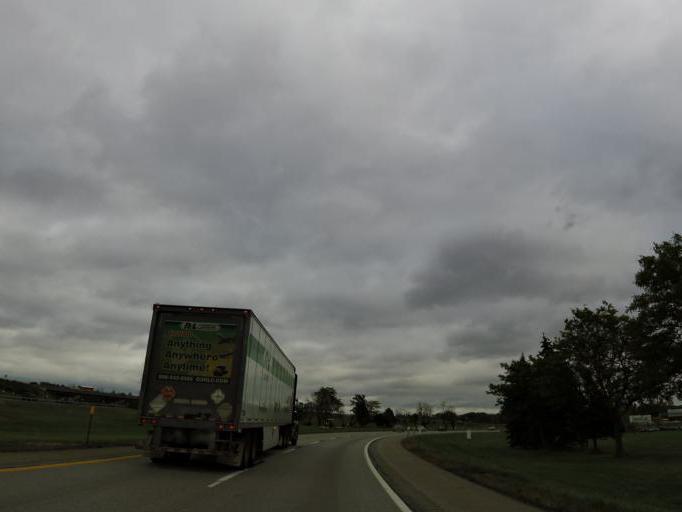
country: US
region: New York
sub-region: Erie County
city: Sloan
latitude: 42.8755
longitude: -78.7913
